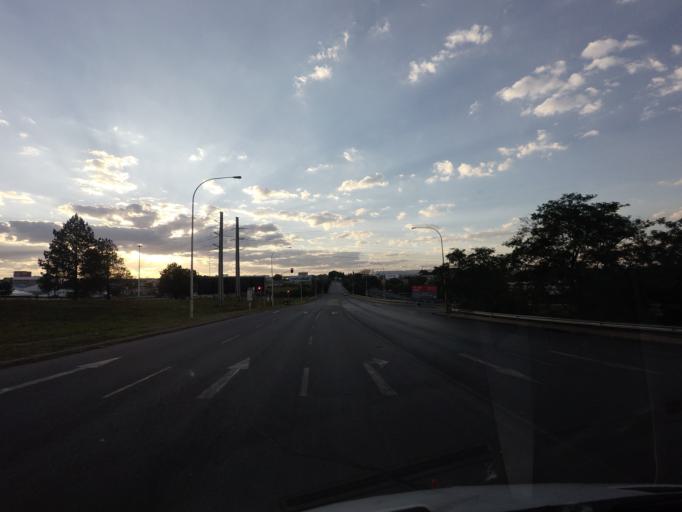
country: ZA
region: Gauteng
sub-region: City of Johannesburg Metropolitan Municipality
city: Modderfontein
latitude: -26.1302
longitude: 28.2212
